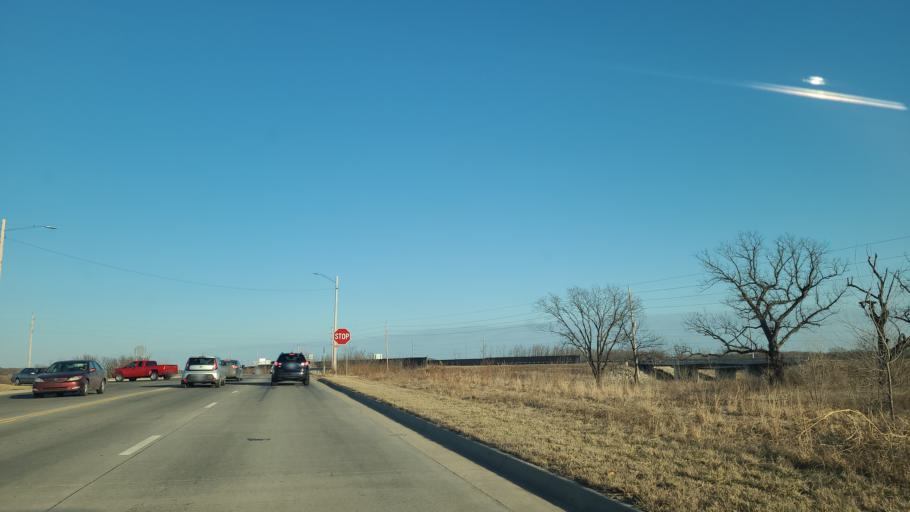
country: US
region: Kansas
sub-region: Douglas County
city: Lawrence
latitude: 38.9279
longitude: -95.2431
